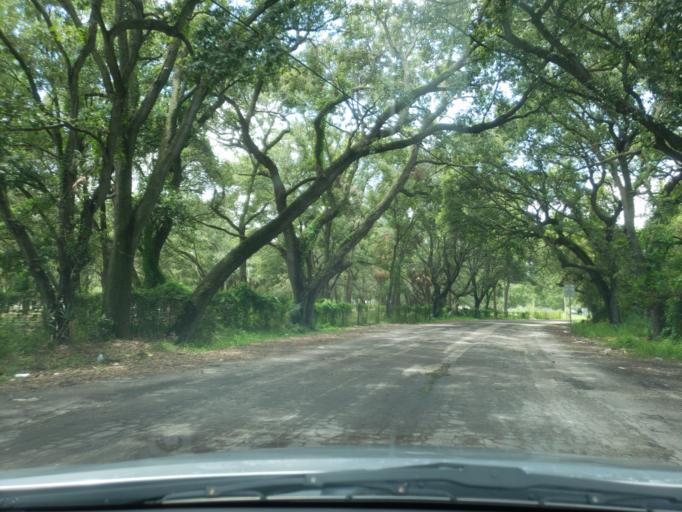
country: US
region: Florida
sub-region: Hillsborough County
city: Palm River-Clair Mel
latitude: 27.9156
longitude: -82.3936
